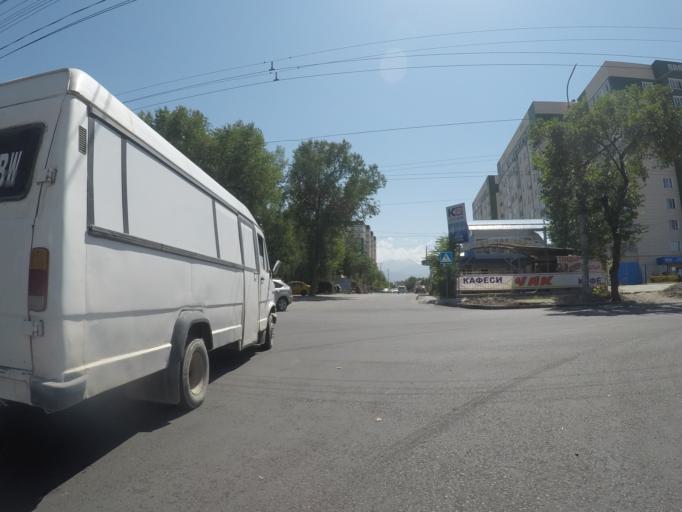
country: KG
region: Chuy
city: Bishkek
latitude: 42.8438
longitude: 74.5768
